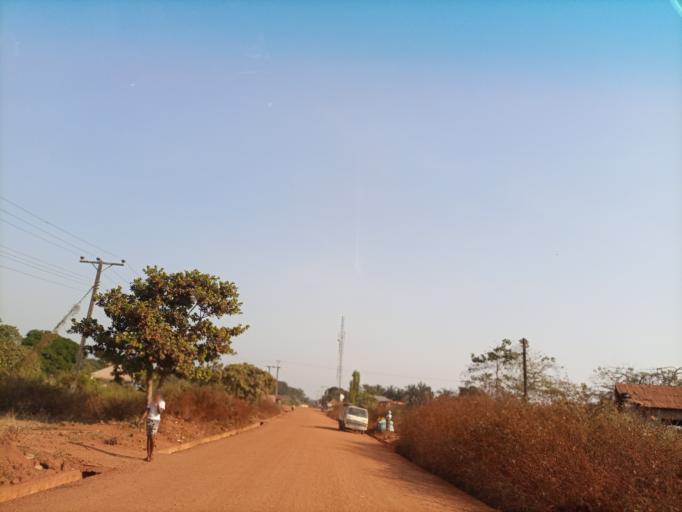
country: NG
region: Enugu
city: Opi
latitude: 6.7474
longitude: 7.4114
